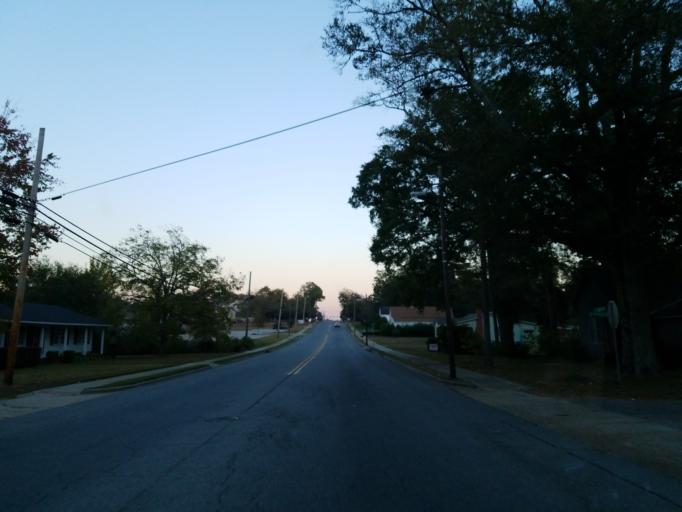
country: US
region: Georgia
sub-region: Irwin County
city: Ocilla
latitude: 31.5943
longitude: -83.2569
